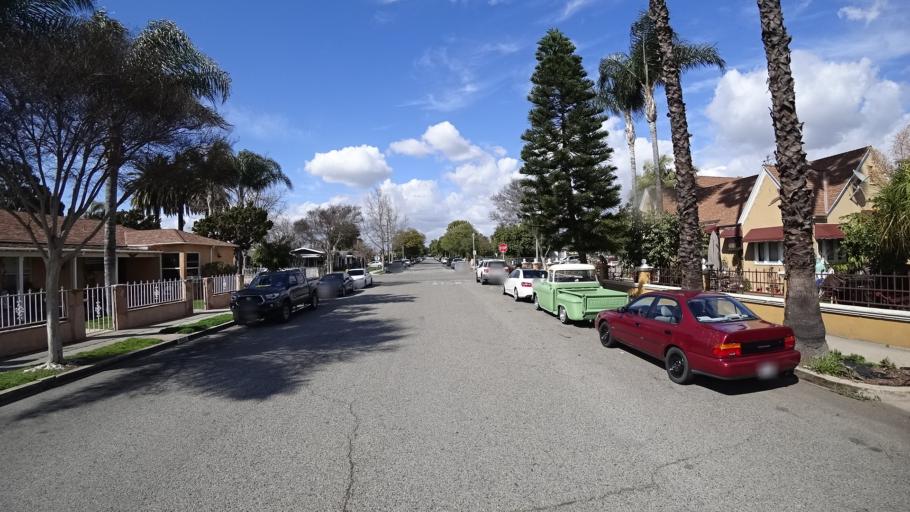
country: US
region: California
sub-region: Orange County
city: Anaheim
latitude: 33.8420
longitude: -117.9147
